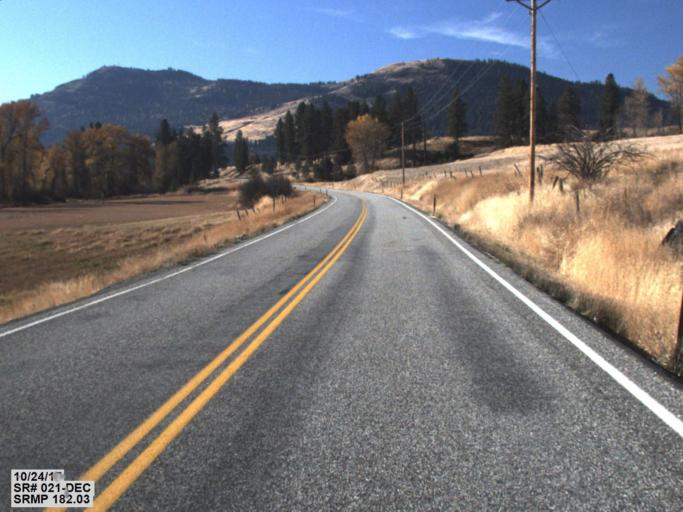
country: CA
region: British Columbia
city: Grand Forks
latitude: 48.8942
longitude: -118.5941
